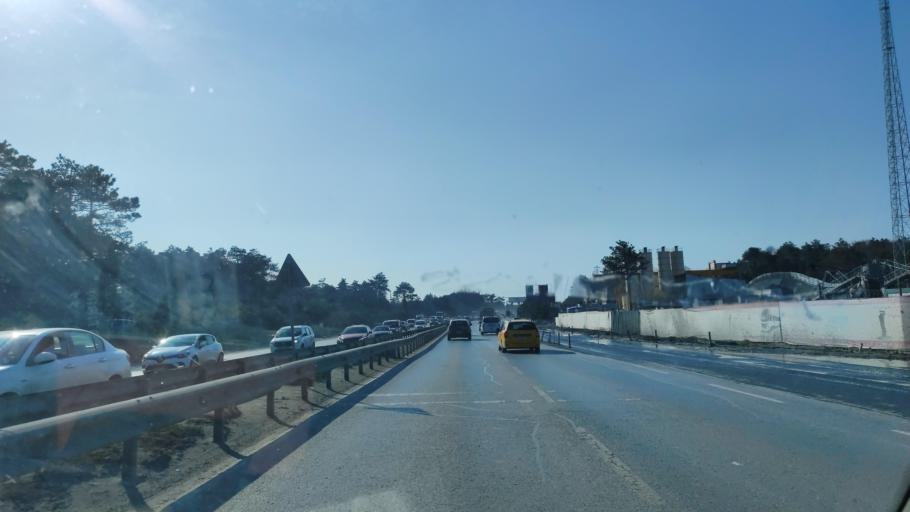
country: TR
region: Istanbul
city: Basaksehir
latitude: 41.1605
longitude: 28.7791
